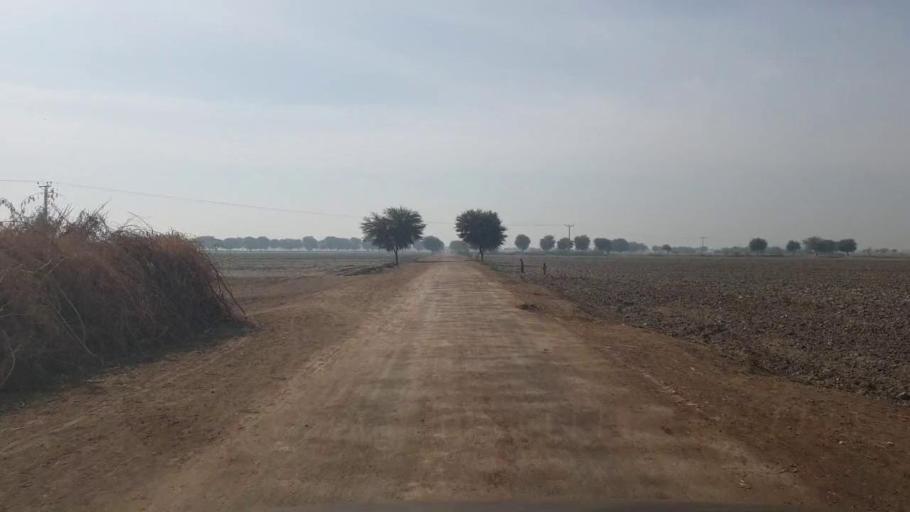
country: PK
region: Sindh
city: Umarkot
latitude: 25.3512
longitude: 69.6765
